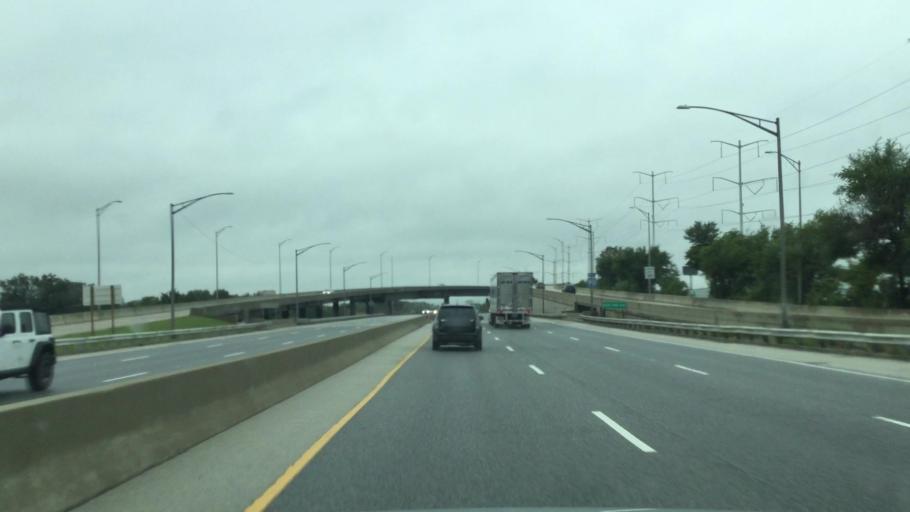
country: US
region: Indiana
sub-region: Lake County
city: Whiting
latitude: 41.7474
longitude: -87.5824
